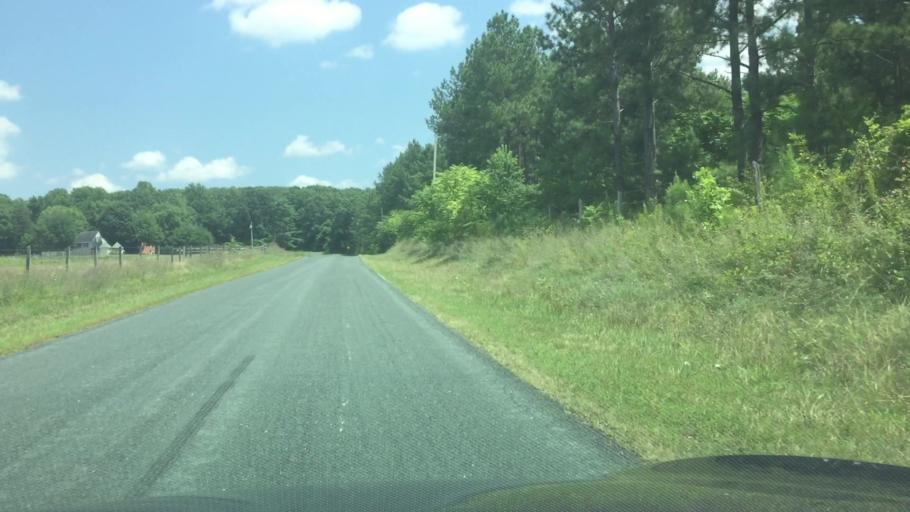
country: US
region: Virginia
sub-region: Appomattox County
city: Appomattox
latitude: 37.3213
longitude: -78.8542
